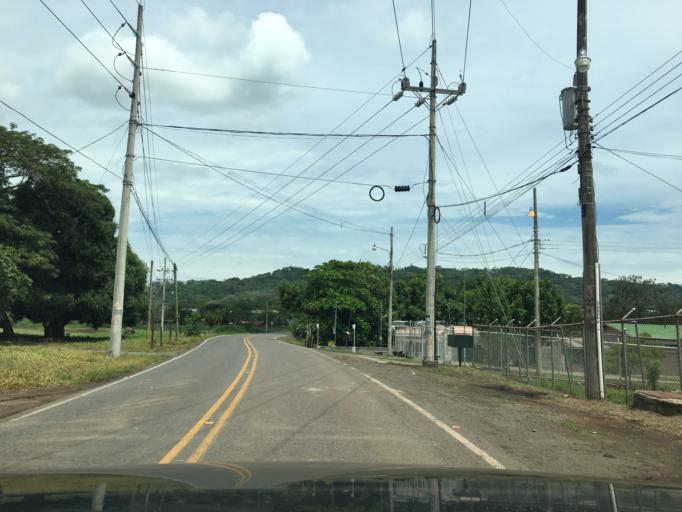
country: CR
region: Puntarenas
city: Esparza
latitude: 9.9300
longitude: -84.6923
